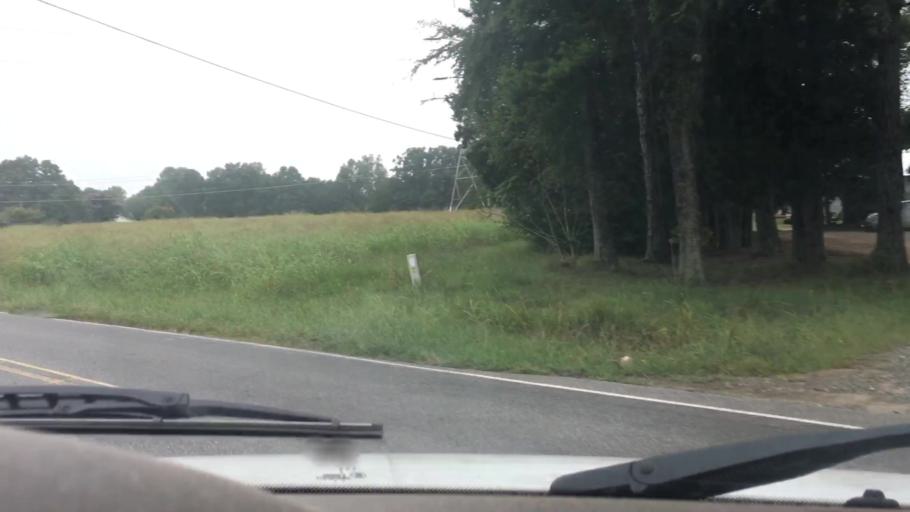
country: US
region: North Carolina
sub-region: Gaston County
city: Davidson
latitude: 35.5264
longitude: -80.7975
